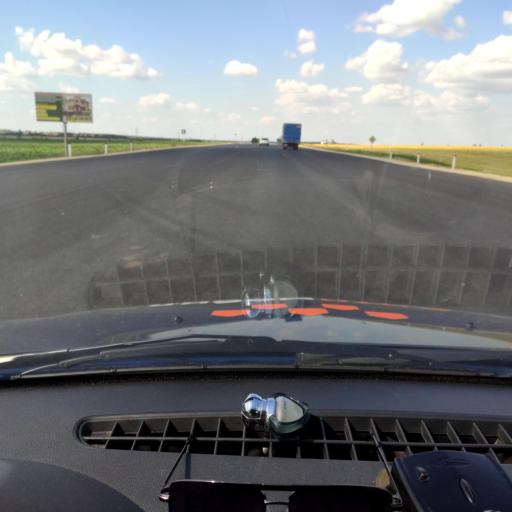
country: RU
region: Voronezj
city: Novovoronezh
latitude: 51.3428
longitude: 39.2772
